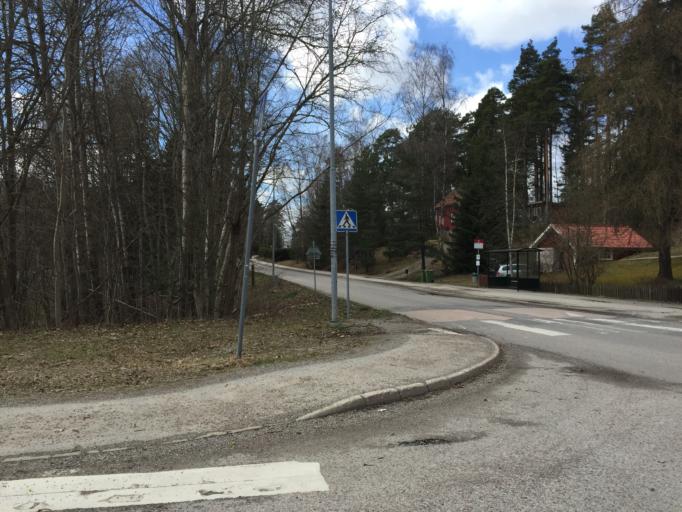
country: SE
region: Stockholm
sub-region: Botkyrka Kommun
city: Tumba
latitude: 59.1911
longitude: 17.8156
